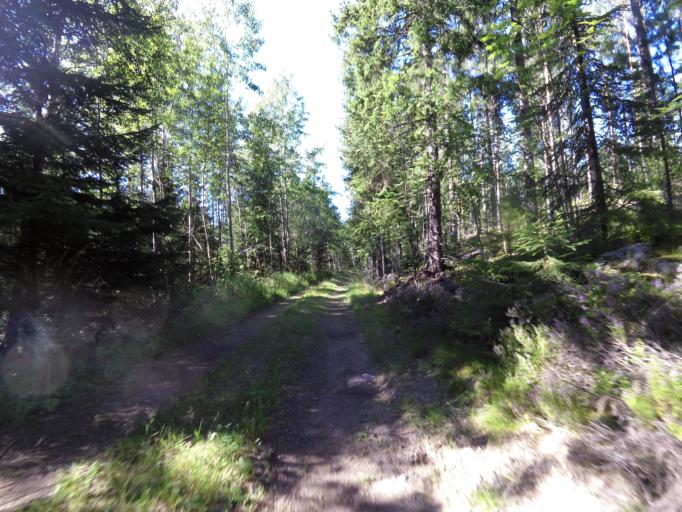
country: SE
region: Gaevleborg
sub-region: Hofors Kommun
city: Hofors
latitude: 60.5674
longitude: 16.4681
